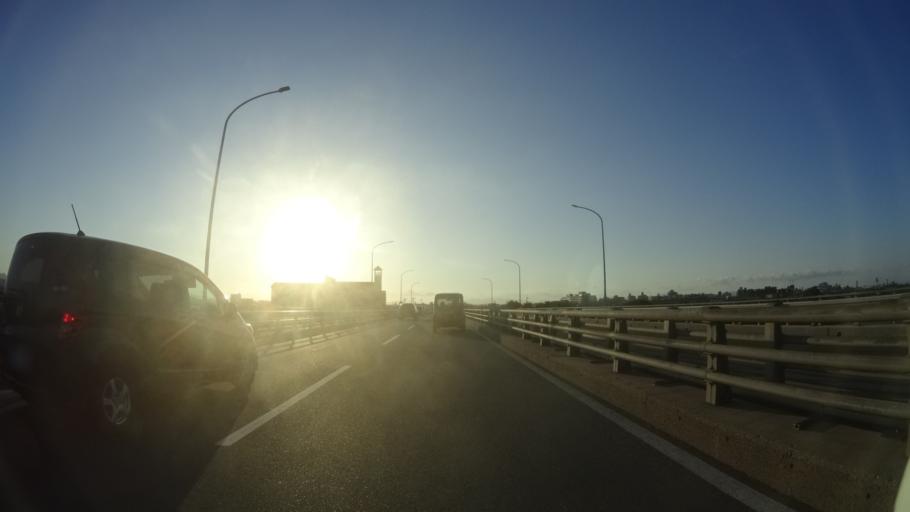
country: JP
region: Tottori
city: Yonago
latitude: 35.4480
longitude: 133.3715
